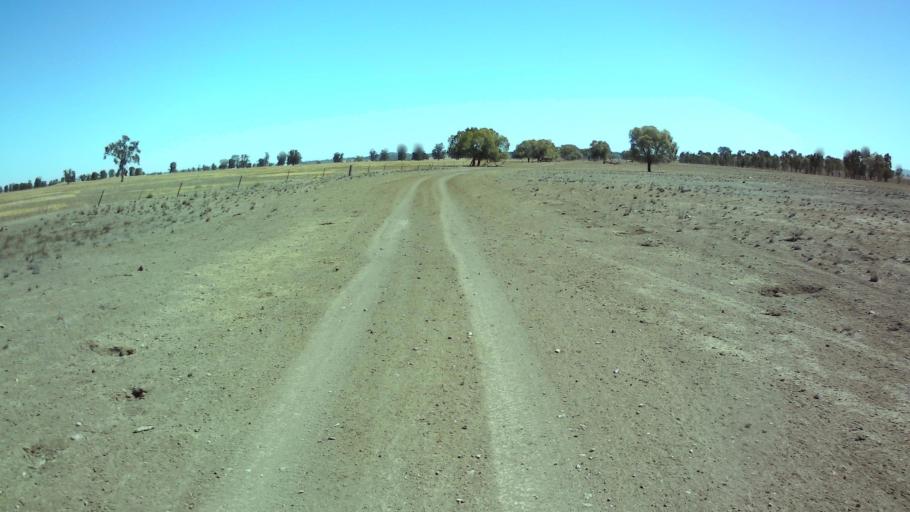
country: AU
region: New South Wales
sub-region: Forbes
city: Forbes
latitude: -33.7204
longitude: 147.6657
